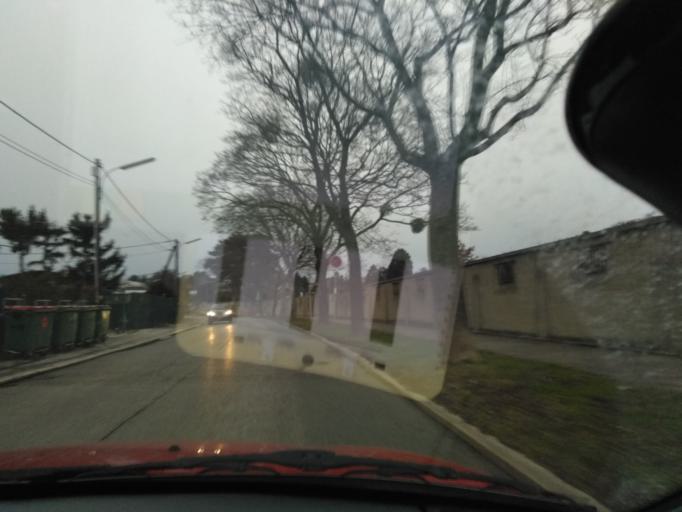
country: AT
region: Vienna
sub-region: Wien Stadt
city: Vienna
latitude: 48.2299
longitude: 16.3179
